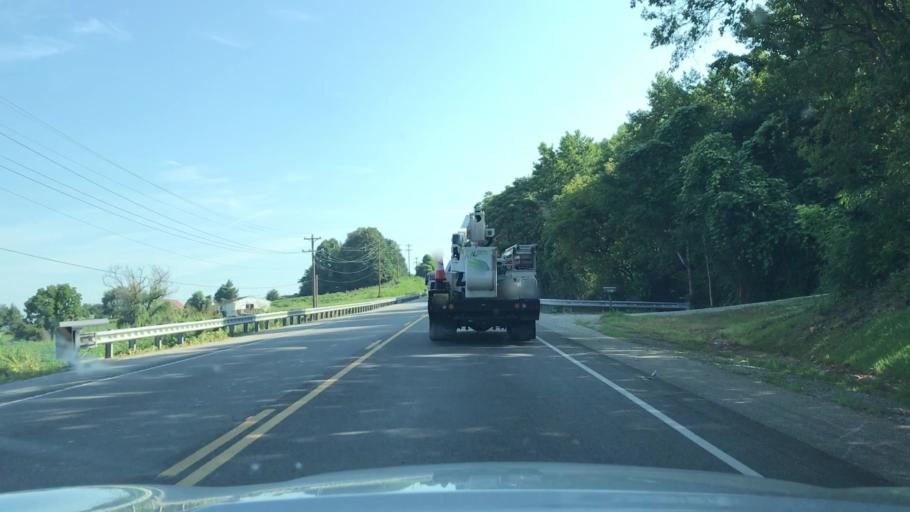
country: US
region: Tennessee
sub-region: Overton County
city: Livingston
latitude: 36.4230
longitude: -85.2828
